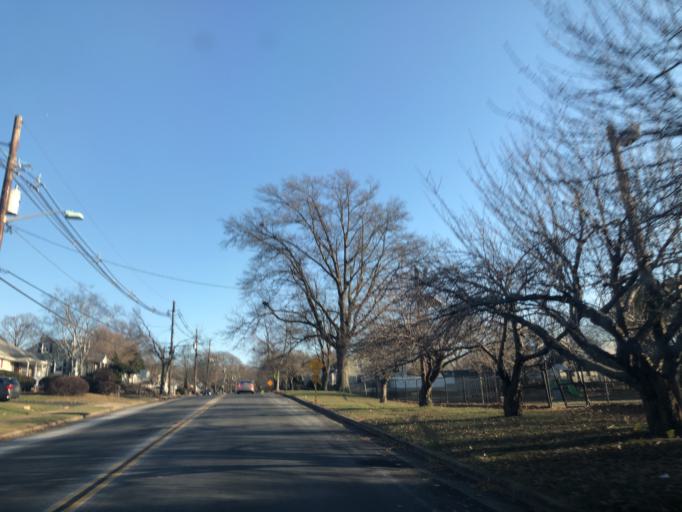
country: US
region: New Jersey
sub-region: Middlesex County
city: Fords
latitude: 40.5394
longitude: -74.3356
